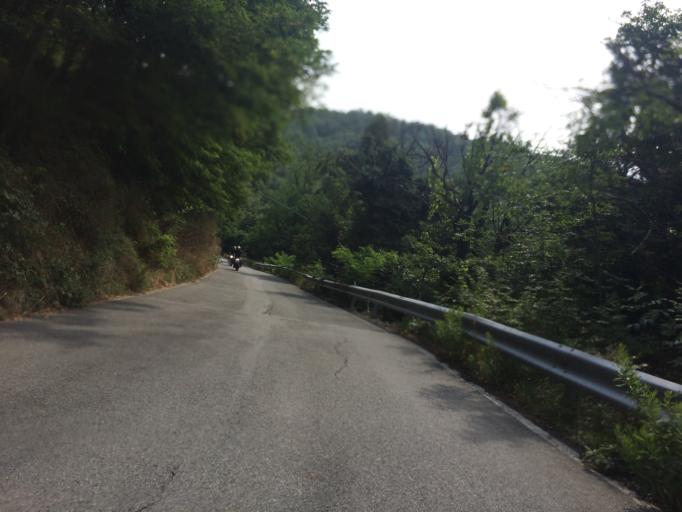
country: IT
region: Liguria
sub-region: Provincia di Savona
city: San Giovanni
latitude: 44.3940
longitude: 8.5090
